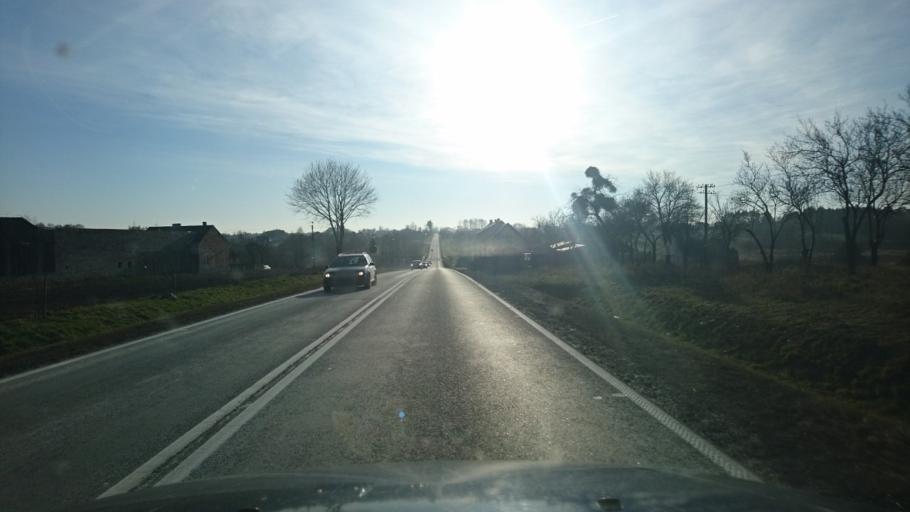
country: PL
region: Opole Voivodeship
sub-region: Powiat oleski
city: Dalachow
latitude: 51.0576
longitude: 18.5992
